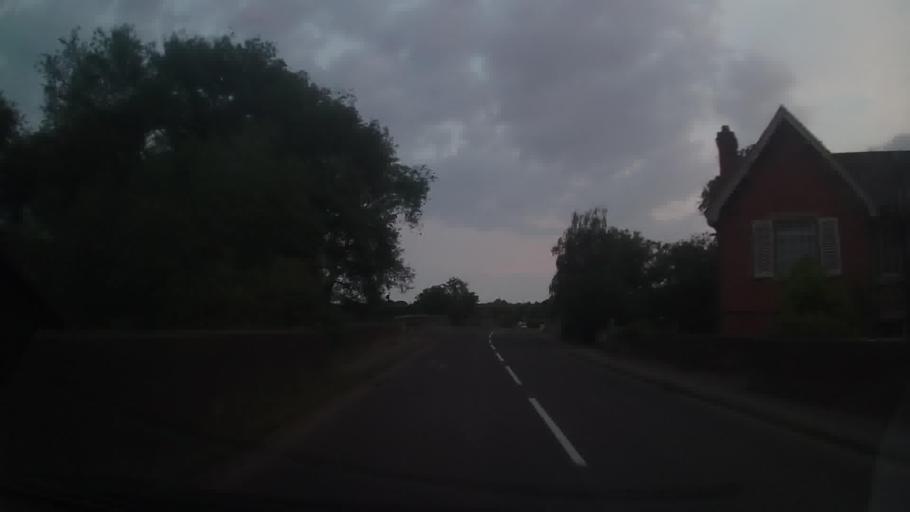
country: GB
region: England
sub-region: Leicestershire
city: Sileby
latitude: 52.7113
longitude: -1.1211
